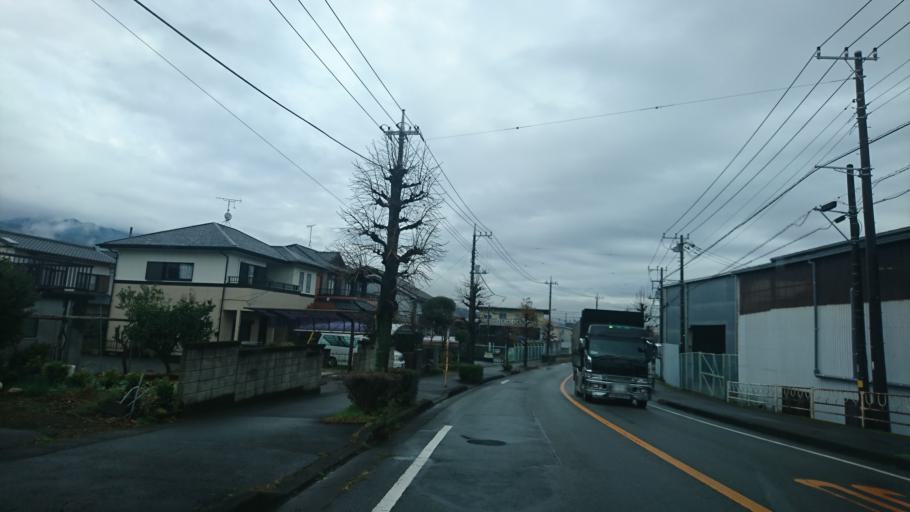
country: JP
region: Shizuoka
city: Fuji
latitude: 35.1581
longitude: 138.7421
